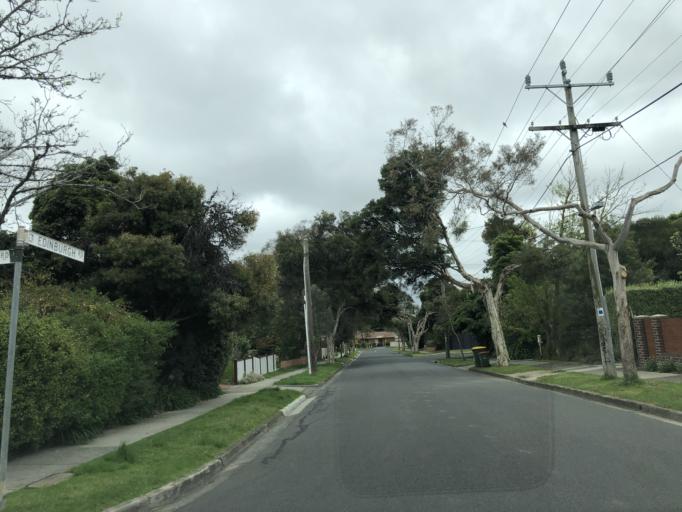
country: AU
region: Victoria
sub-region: Whitehorse
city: Blackburn South
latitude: -37.8369
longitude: 145.1403
